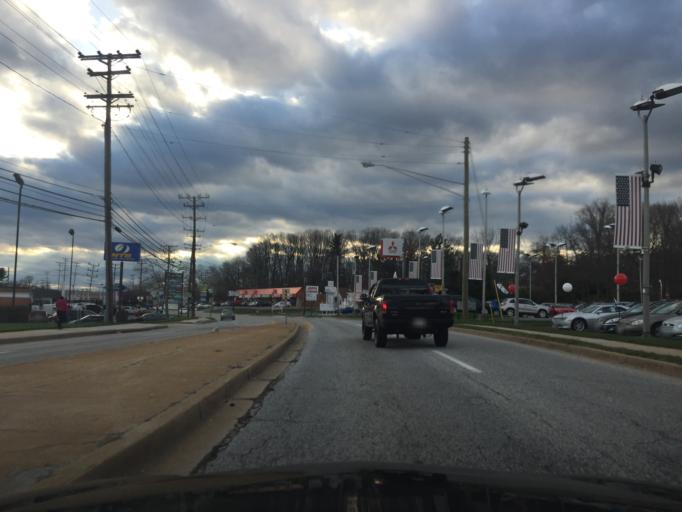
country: US
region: Maryland
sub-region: Baltimore County
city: Parkville
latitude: 39.4004
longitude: -76.5487
